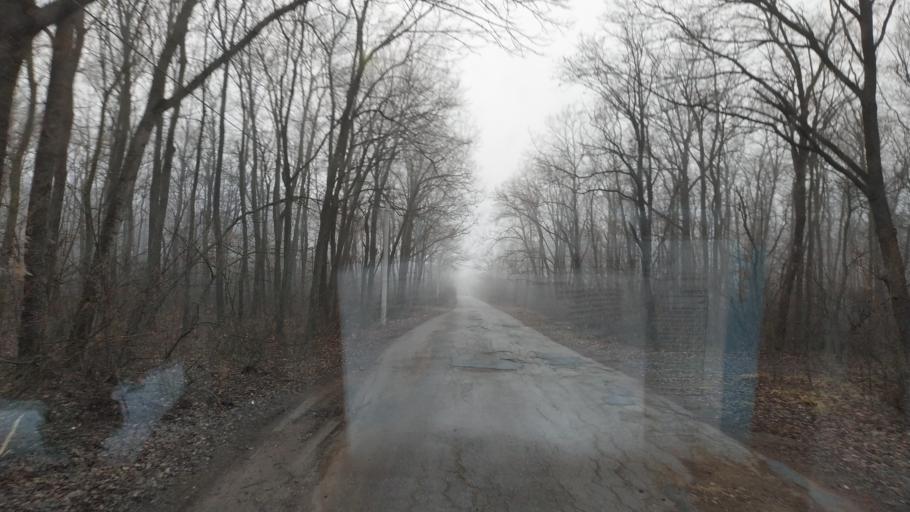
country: MD
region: Laloveni
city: Ialoveni
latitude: 46.9459
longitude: 28.7024
